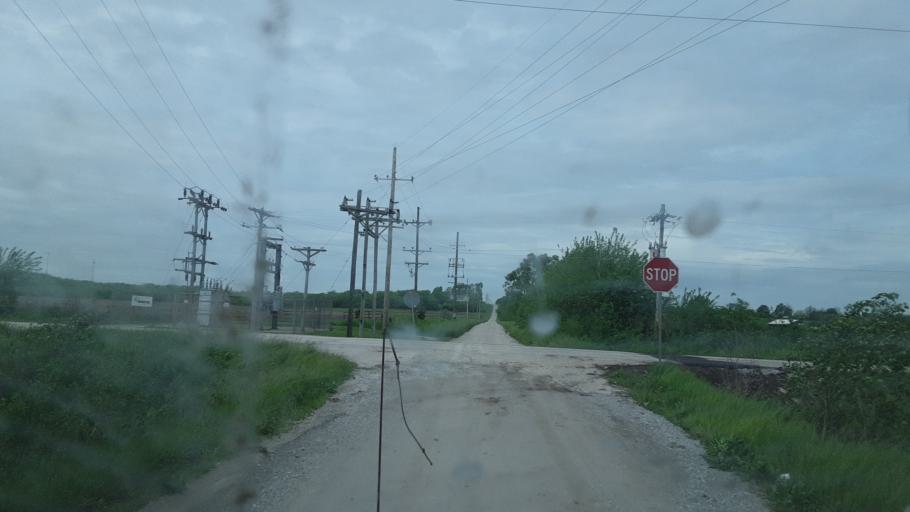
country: US
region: Missouri
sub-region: Clark County
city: Kahoka
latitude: 40.4236
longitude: -91.5777
